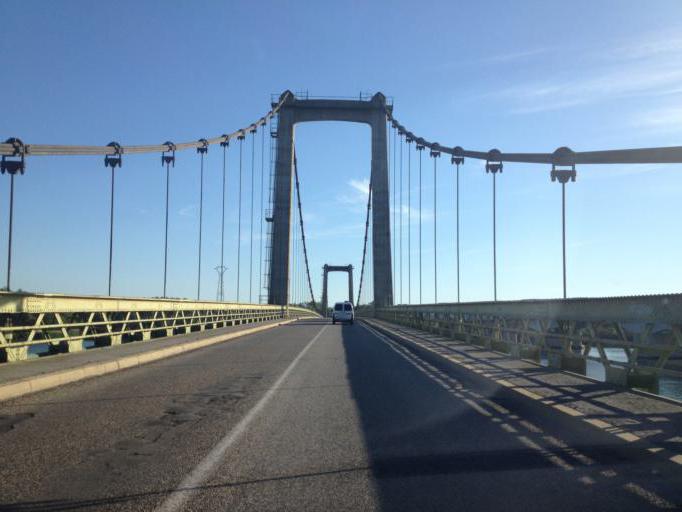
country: FR
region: Languedoc-Roussillon
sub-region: Departement du Gard
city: Montfaucon
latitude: 44.0731
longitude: 4.7696
